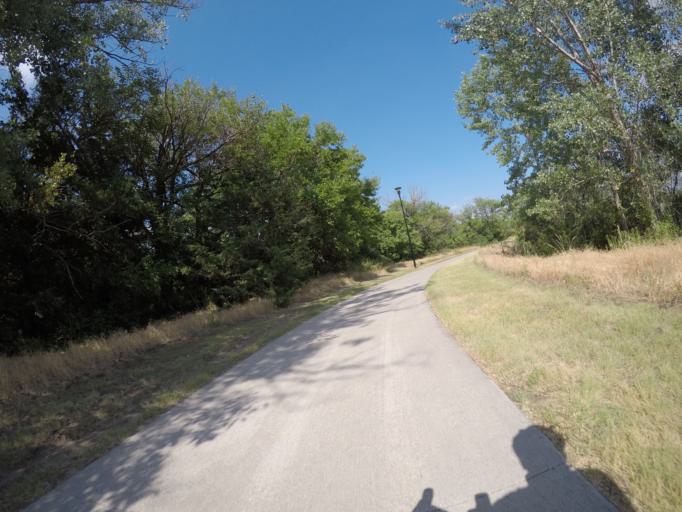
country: US
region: Nebraska
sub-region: Buffalo County
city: Kearney
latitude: 40.6771
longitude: -99.0961
